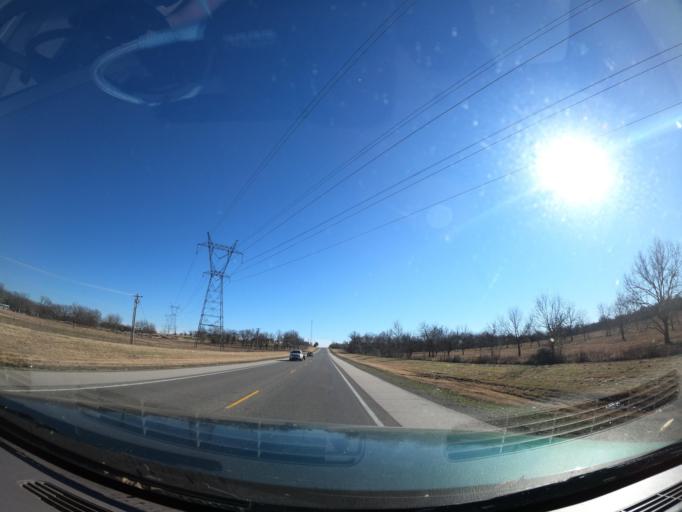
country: US
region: Oklahoma
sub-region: Muskogee County
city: Haskell
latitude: 35.7819
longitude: -95.6623
